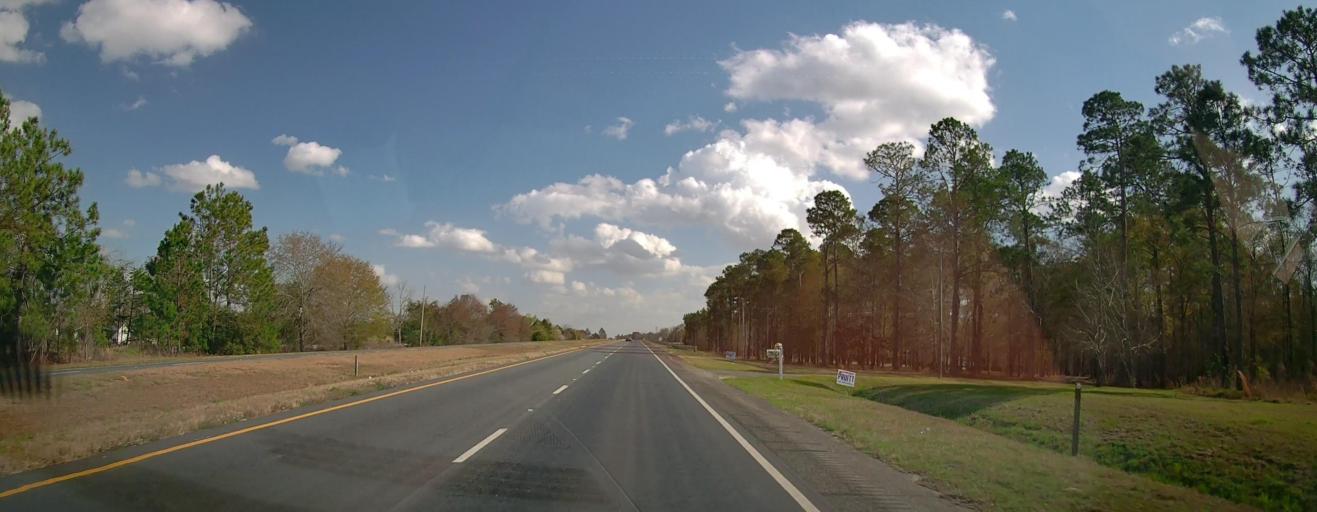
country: US
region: Georgia
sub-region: Dodge County
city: Eastman
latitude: 32.1304
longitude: -83.1230
